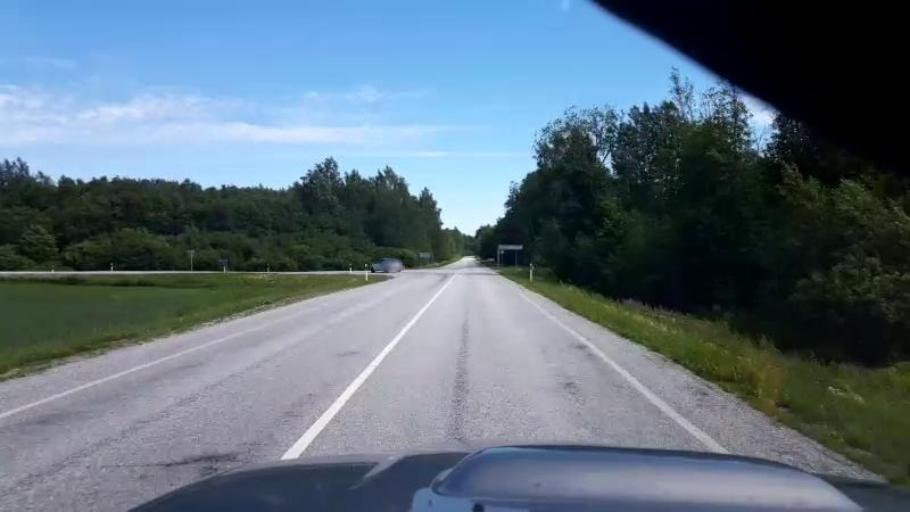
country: EE
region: Laeaene-Virumaa
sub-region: Rakke vald
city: Rakke
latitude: 58.9163
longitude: 26.2595
